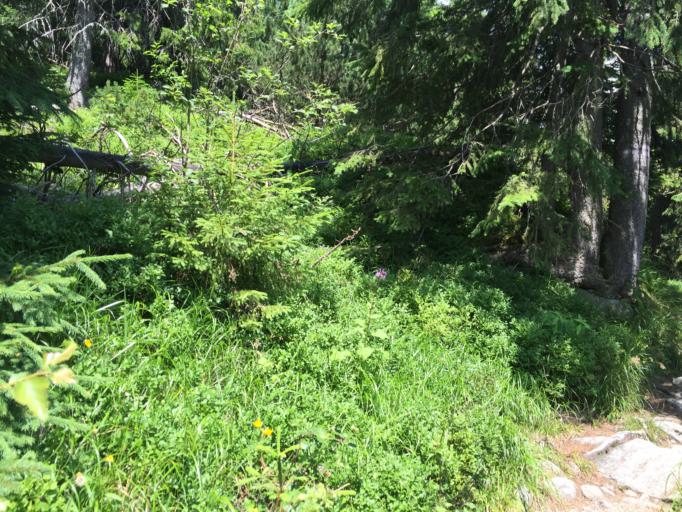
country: SK
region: Presovsky
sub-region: Okres Poprad
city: Vysoke Tatry
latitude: 49.1582
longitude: 20.2121
